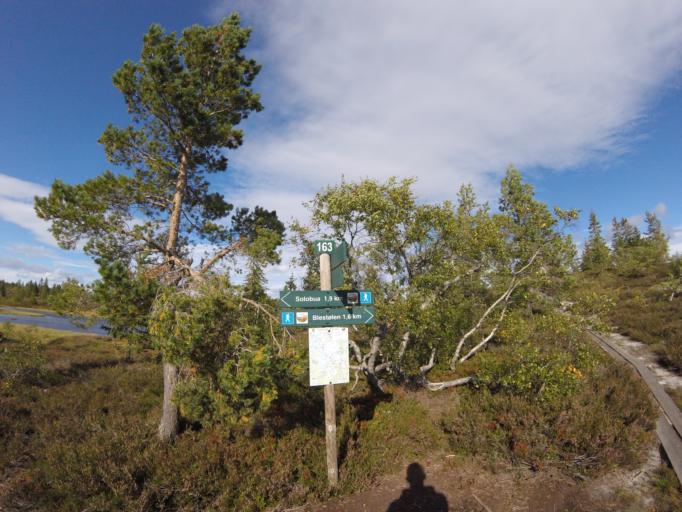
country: NO
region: Buskerud
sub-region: Flesberg
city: Lampeland
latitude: 59.7631
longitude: 9.4193
